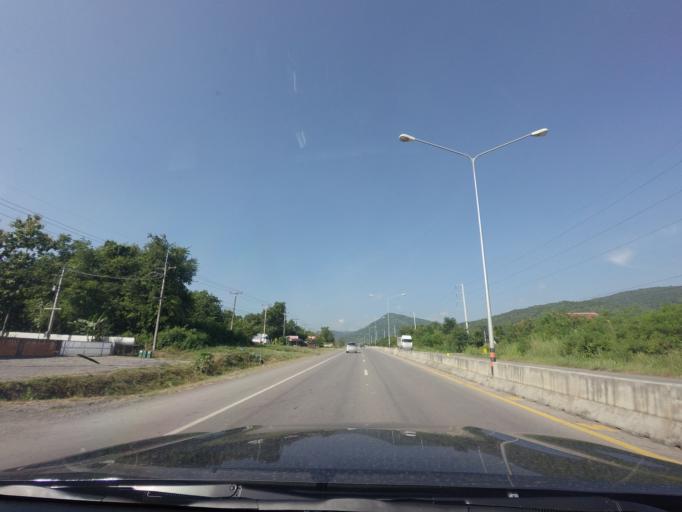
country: TH
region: Phetchabun
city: Lom Sak
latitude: 16.7668
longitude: 101.1599
